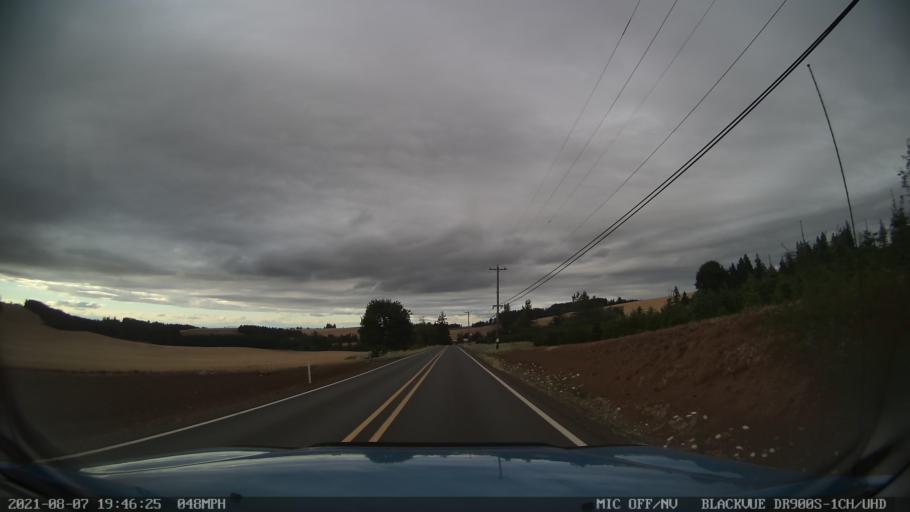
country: US
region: Oregon
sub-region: Marion County
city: Silverton
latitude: 44.9588
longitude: -122.7017
